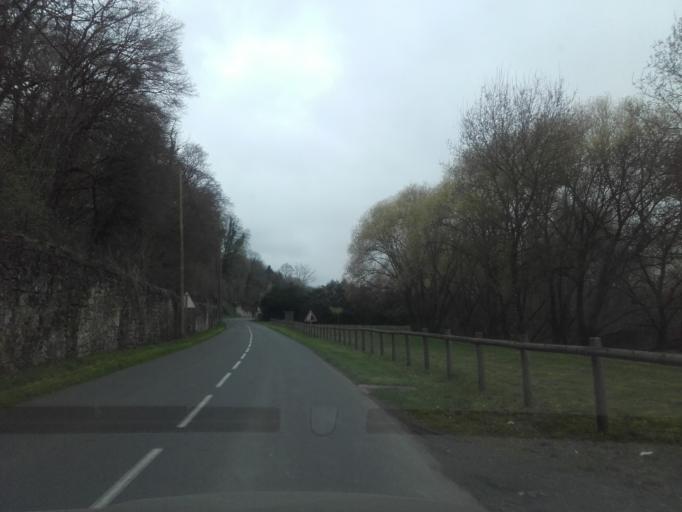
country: FR
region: Centre
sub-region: Departement d'Indre-et-Loire
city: Huismes
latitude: 47.2497
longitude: 0.2871
